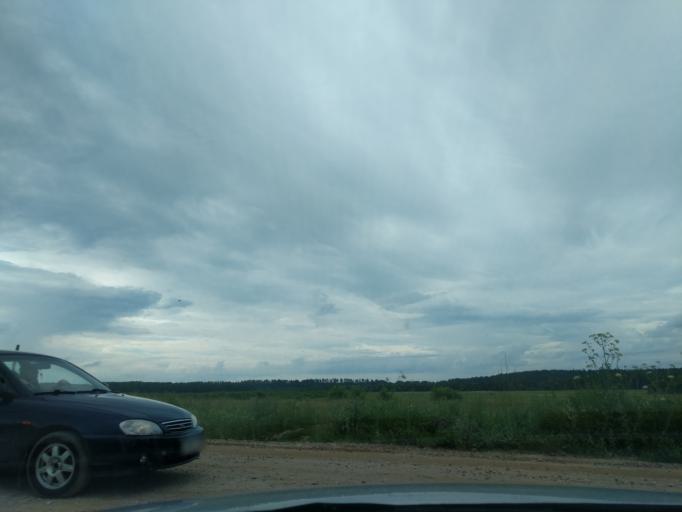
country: RU
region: Kaluga
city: Nikola-Lenivets
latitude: 54.7511
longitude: 35.6299
